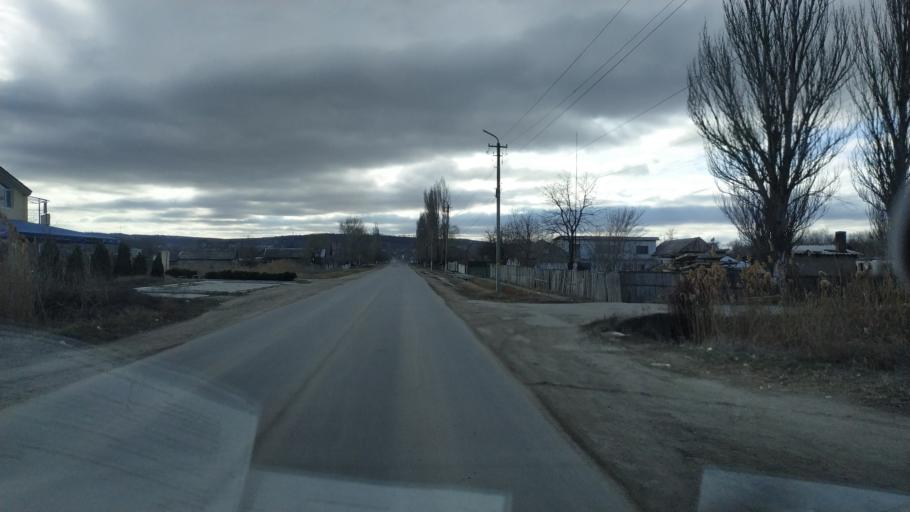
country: MD
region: Causeni
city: Causeni
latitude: 46.6537
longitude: 29.4117
